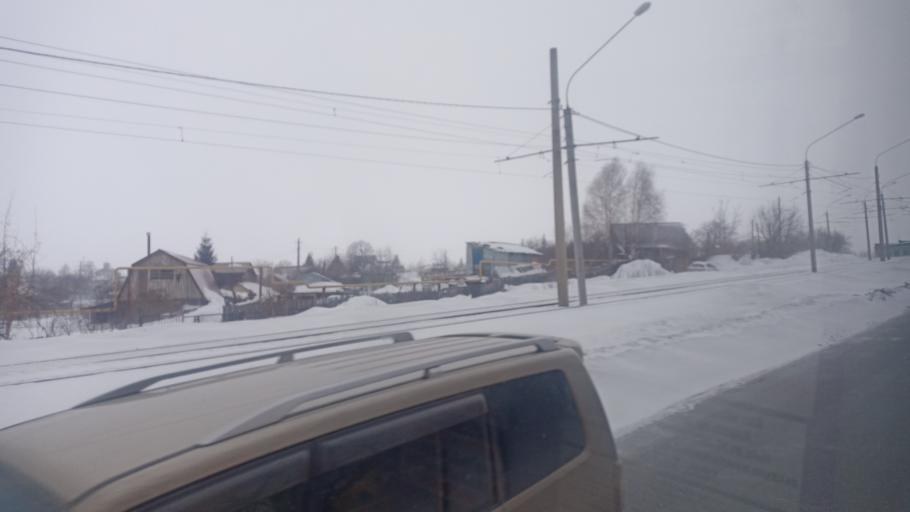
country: RU
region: Altai Krai
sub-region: Gorod Barnaulskiy
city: Barnaul
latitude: 53.3893
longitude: 83.6781
